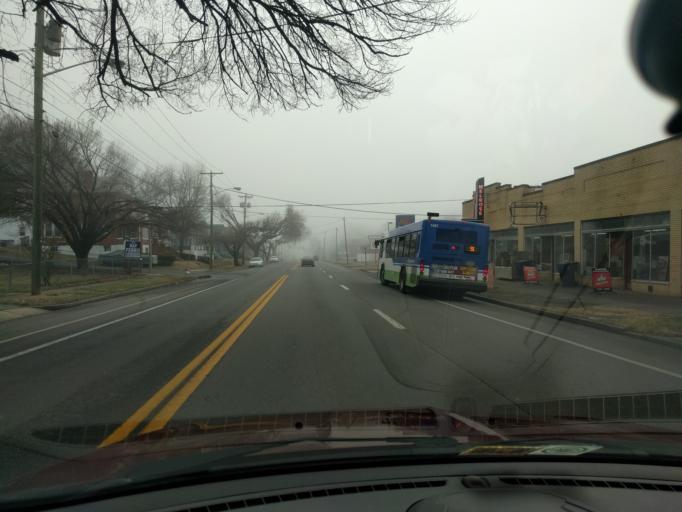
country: US
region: Virginia
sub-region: City of Roanoke
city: Roanoke
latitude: 37.2861
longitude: -79.9744
